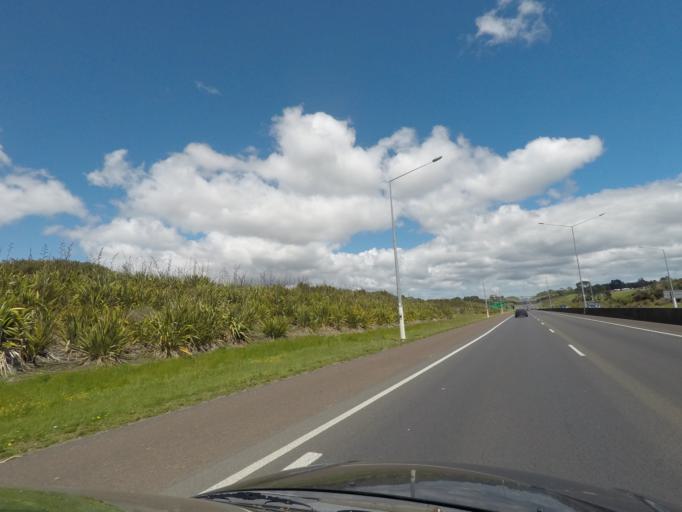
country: NZ
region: Auckland
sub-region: Auckland
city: Rosebank
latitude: -36.8028
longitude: 174.6325
